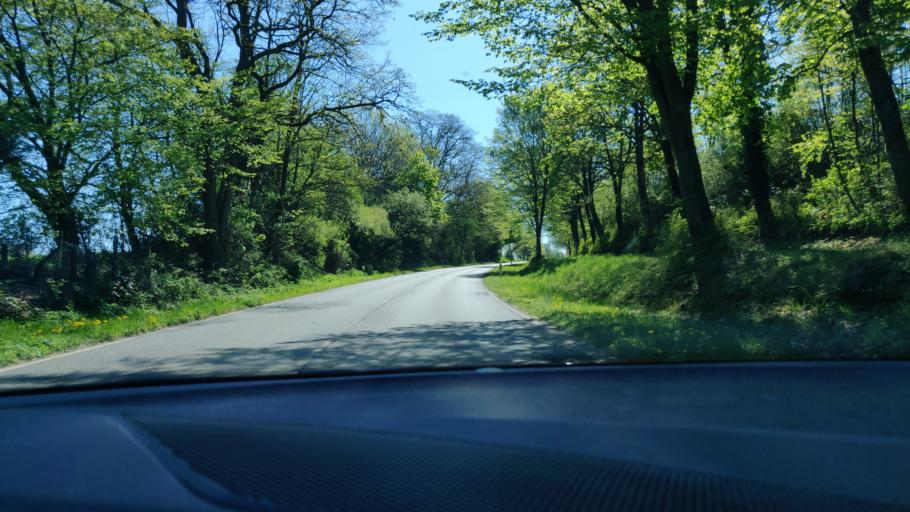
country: DE
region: North Rhine-Westphalia
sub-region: Regierungsbezirk Dusseldorf
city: Mettmann
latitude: 51.2364
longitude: 6.9925
